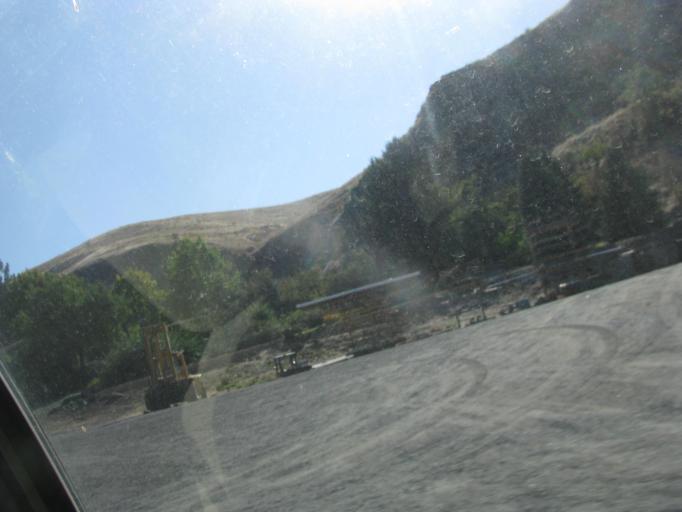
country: US
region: Washington
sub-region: Asotin County
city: Asotin
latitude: 46.3470
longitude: -117.0620
